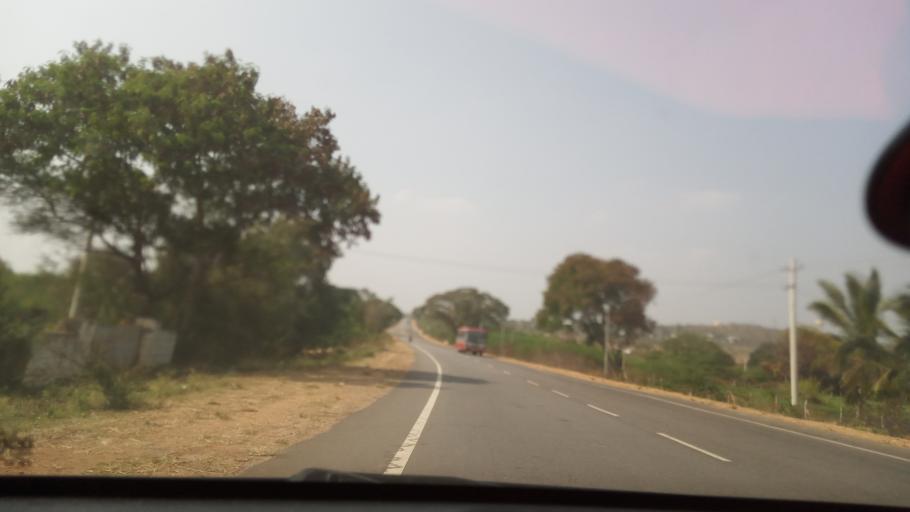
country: IN
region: Karnataka
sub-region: Mysore
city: Nanjangud
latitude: 12.0883
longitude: 76.7285
